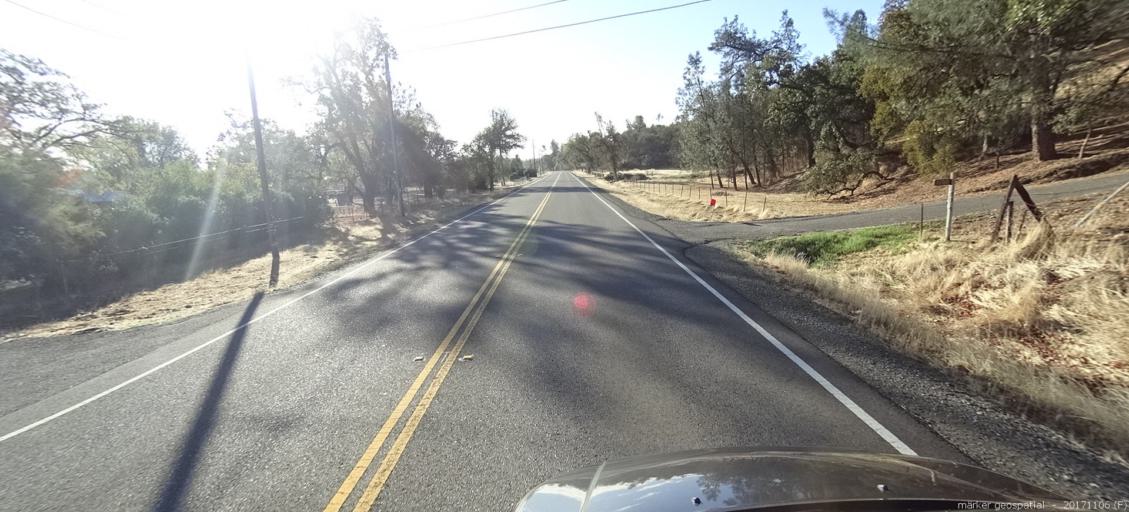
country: US
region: California
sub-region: Shasta County
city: Bella Vista
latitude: 40.6303
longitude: -122.2363
